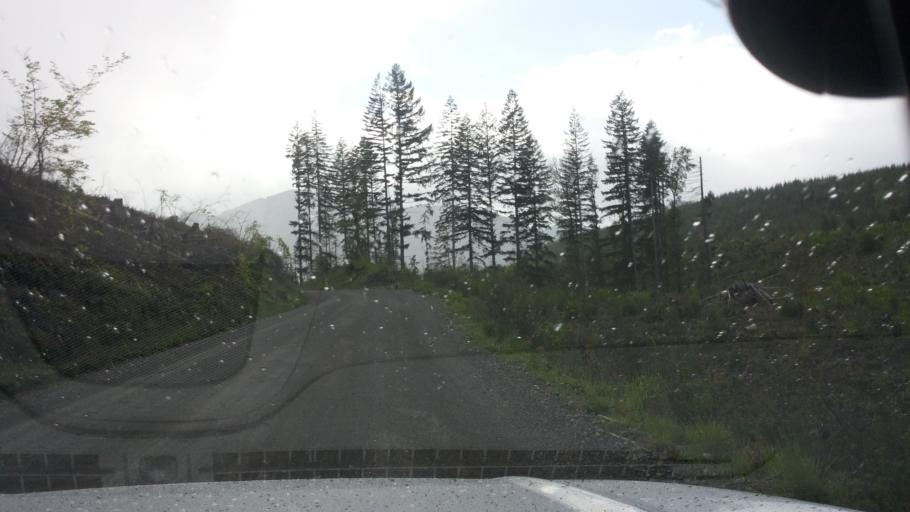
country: US
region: Washington
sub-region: Mason County
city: Shelton
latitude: 47.3388
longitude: -123.2867
